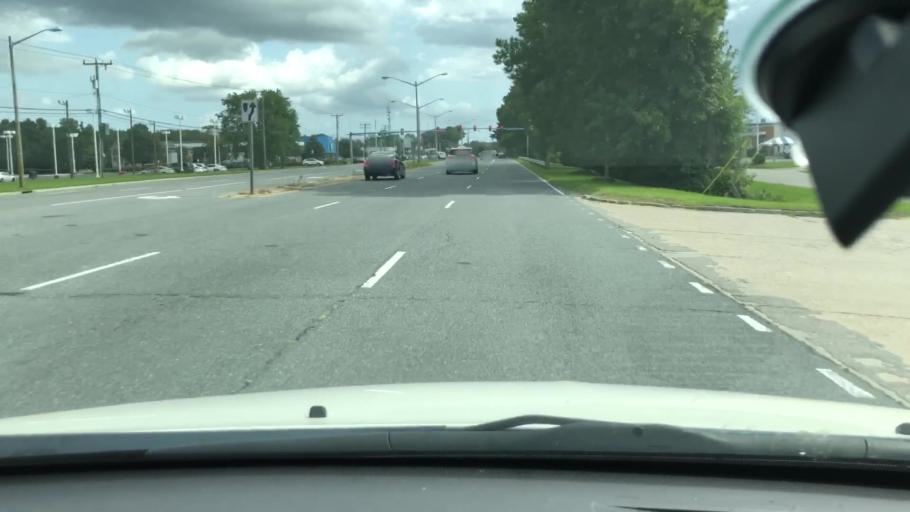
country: US
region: Virginia
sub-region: City of Chesapeake
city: Chesapeake
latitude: 36.7894
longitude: -76.2471
